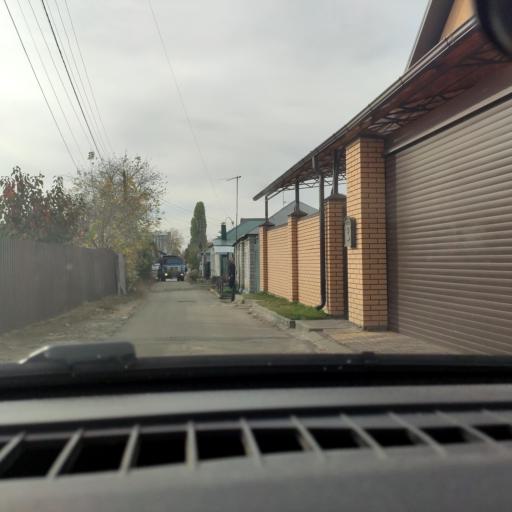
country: RU
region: Voronezj
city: Voronezh
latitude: 51.6483
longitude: 39.1803
